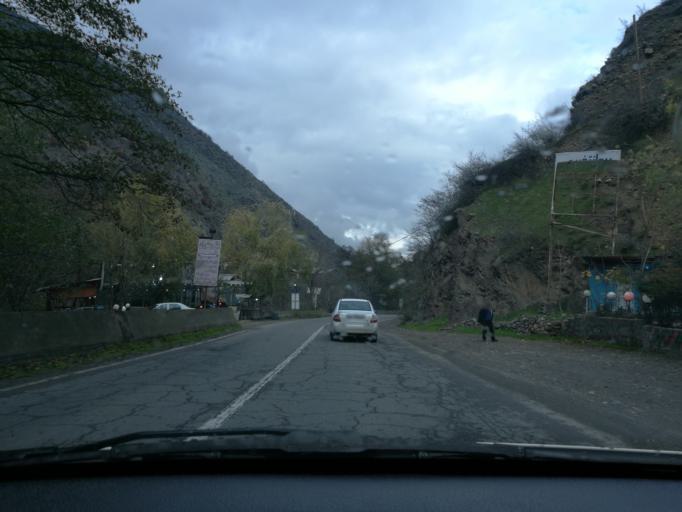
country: IR
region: Mazandaran
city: Chalus
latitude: 36.3285
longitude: 51.2549
